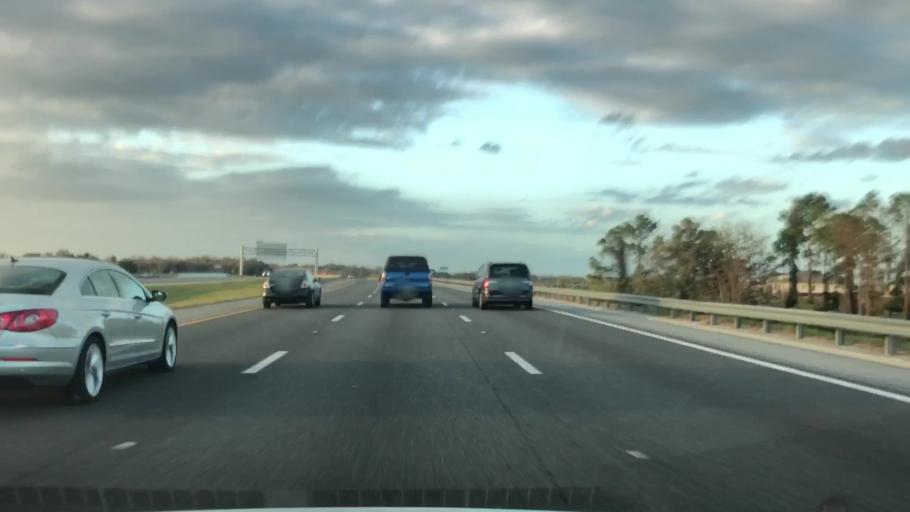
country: US
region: Florida
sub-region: Orange County
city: Apopka
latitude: 28.6678
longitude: -81.5546
